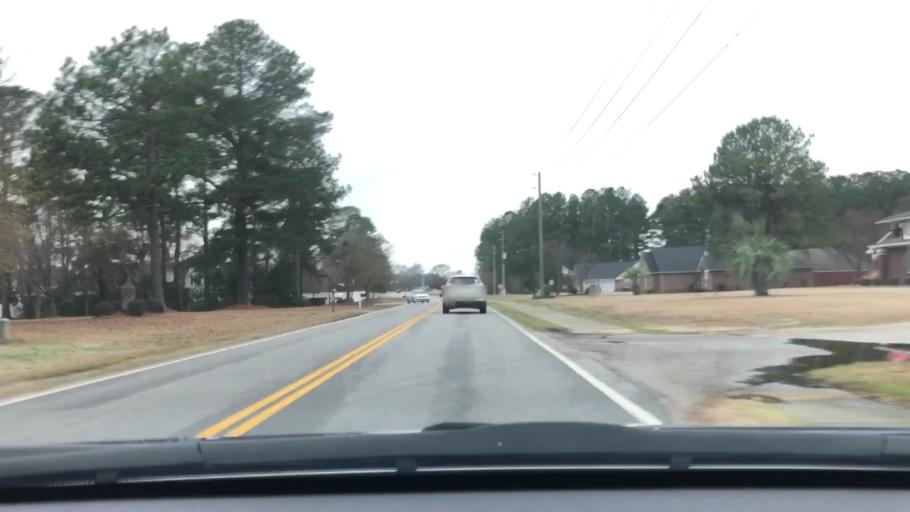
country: US
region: South Carolina
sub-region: Sumter County
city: Cherryvale
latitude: 33.9367
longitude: -80.4154
